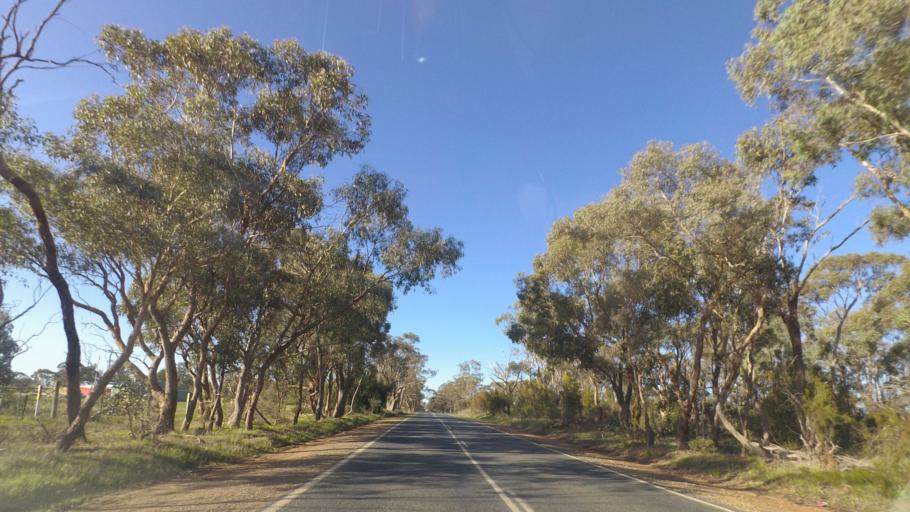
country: AU
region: Victoria
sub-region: Greater Bendigo
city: Epsom
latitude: -36.6771
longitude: 144.3873
